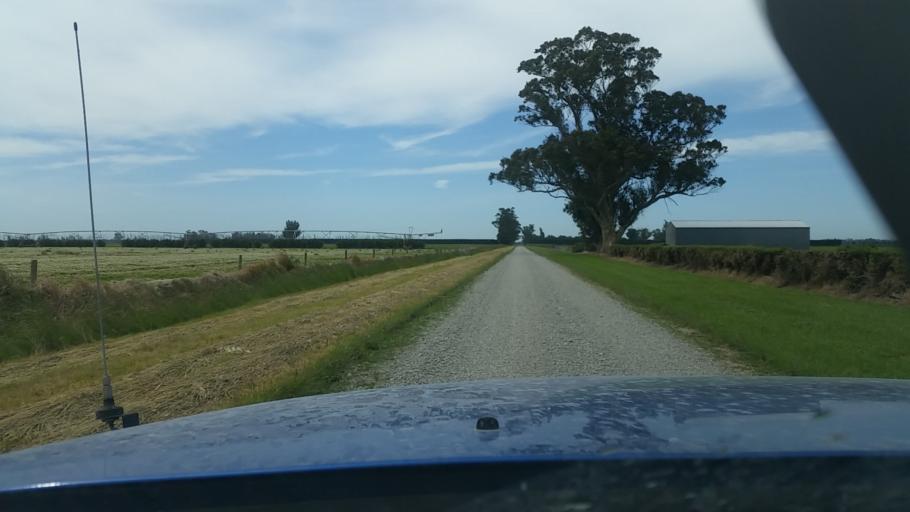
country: NZ
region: Canterbury
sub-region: Ashburton District
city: Tinwald
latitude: -44.0513
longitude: 171.7725
